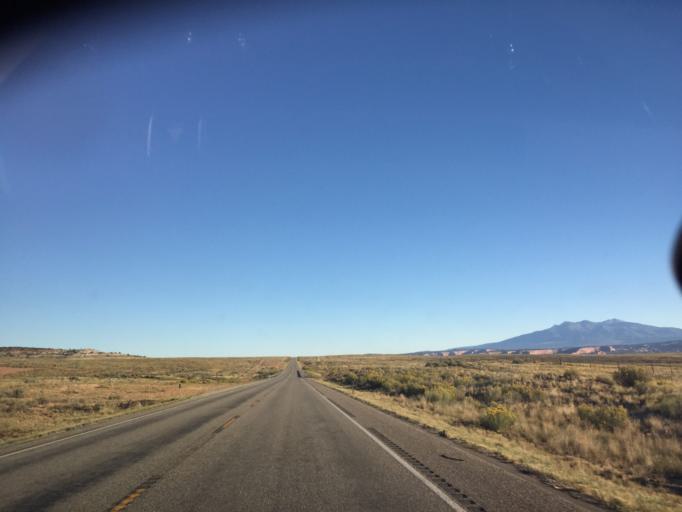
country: US
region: Utah
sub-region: San Juan County
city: Monticello
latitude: 38.1142
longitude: -109.3651
